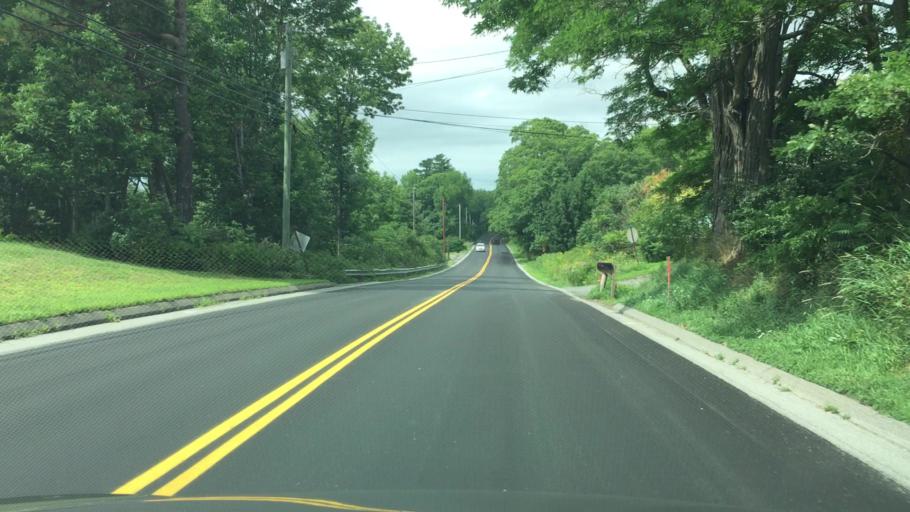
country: US
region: Maine
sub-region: Waldo County
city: Winterport
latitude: 44.6092
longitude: -68.8215
